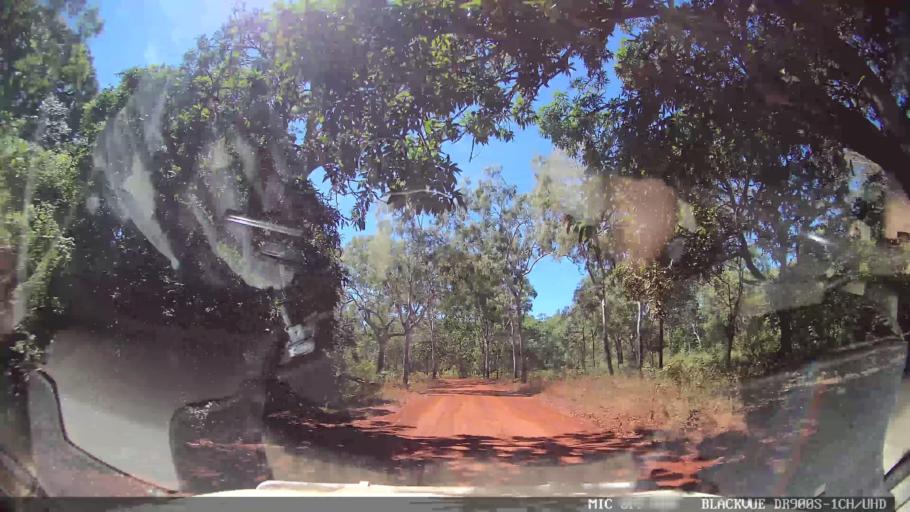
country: AU
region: Queensland
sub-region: Torres
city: Thursday Island
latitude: -10.7794
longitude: 142.4857
